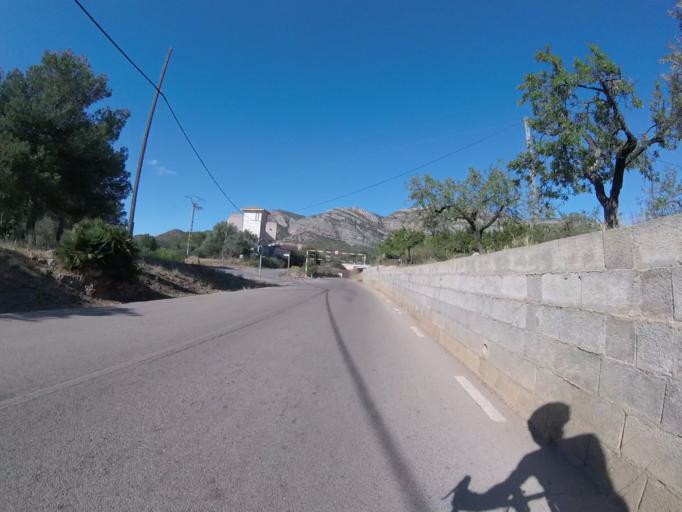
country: ES
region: Valencia
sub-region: Provincia de Castello
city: Orpesa/Oropesa del Mar
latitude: 40.0909
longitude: 0.1295
